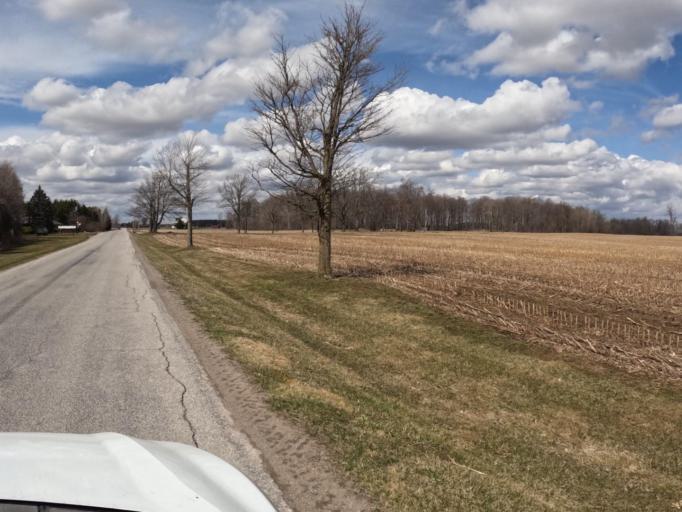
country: CA
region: Ontario
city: Norfolk County
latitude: 42.9045
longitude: -80.1912
